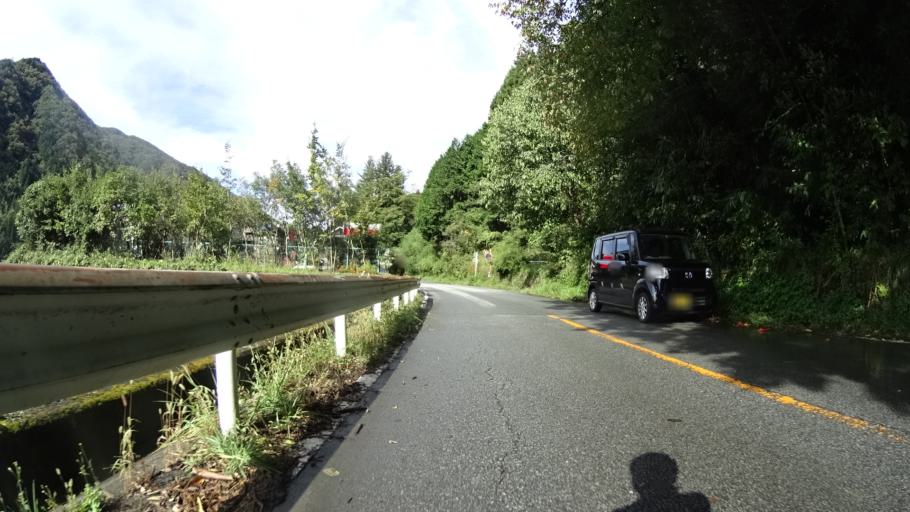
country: JP
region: Yamanashi
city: Otsuki
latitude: 35.7939
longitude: 138.9148
